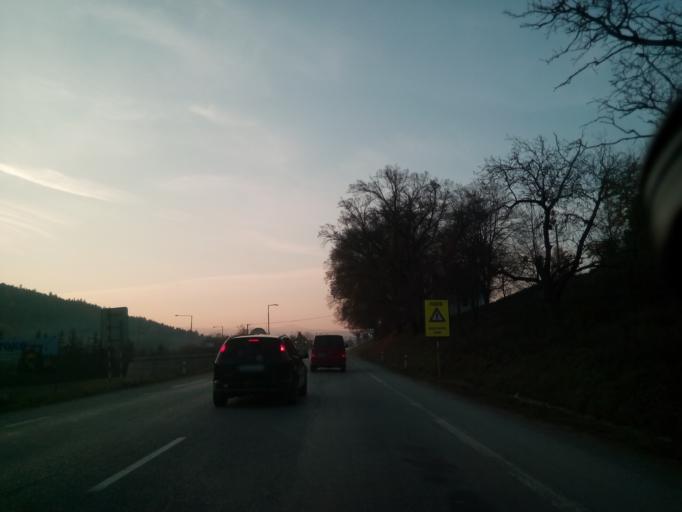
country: SK
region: Presovsky
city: Sabinov
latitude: 49.0203
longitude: 21.0324
